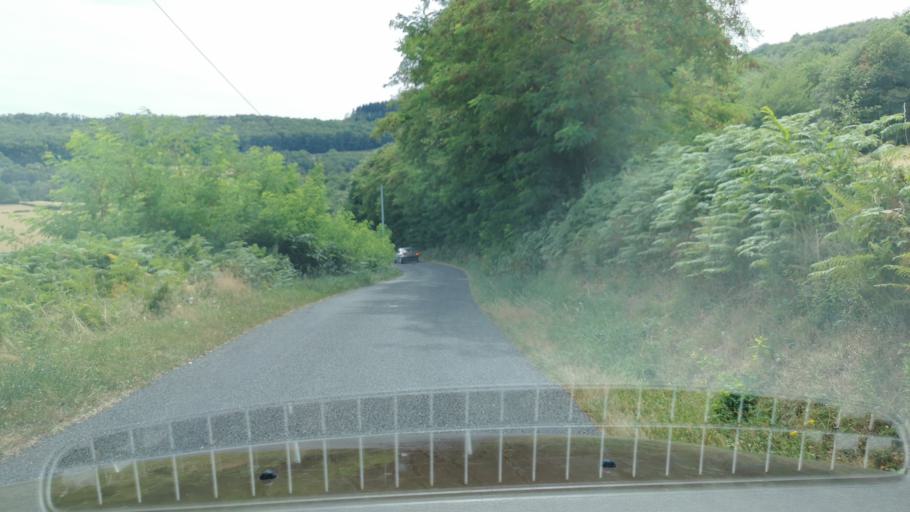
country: FR
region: Bourgogne
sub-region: Departement de Saone-et-Loire
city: Marmagne
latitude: 46.8080
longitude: 4.3084
